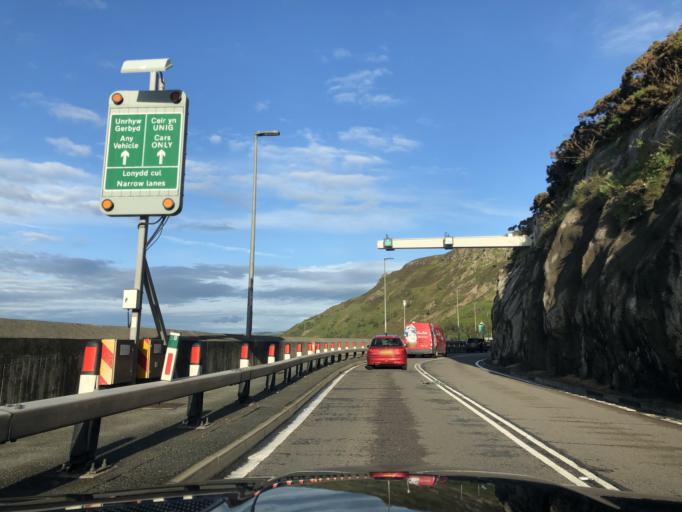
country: GB
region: Wales
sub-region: Conwy
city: Conwy
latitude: 53.2890
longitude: -3.8788
